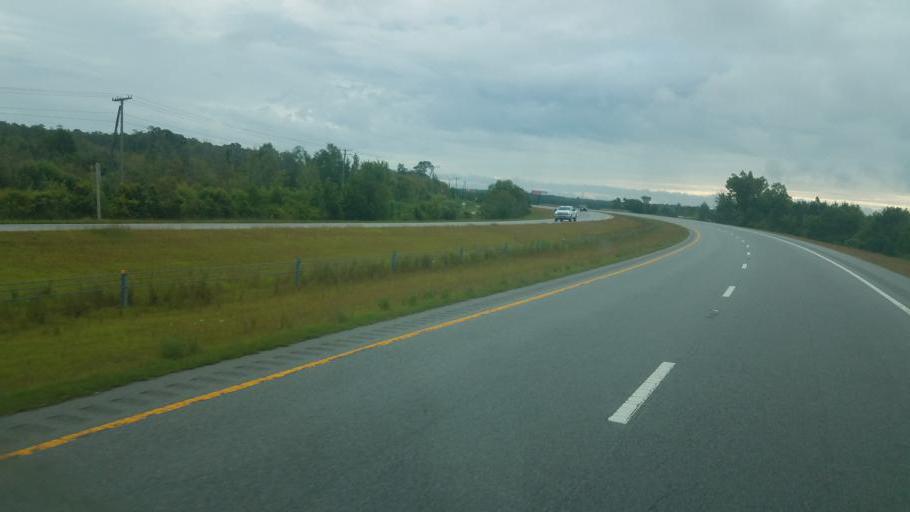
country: US
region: North Carolina
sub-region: Tyrrell County
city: Columbia
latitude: 35.9031
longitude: -76.3040
